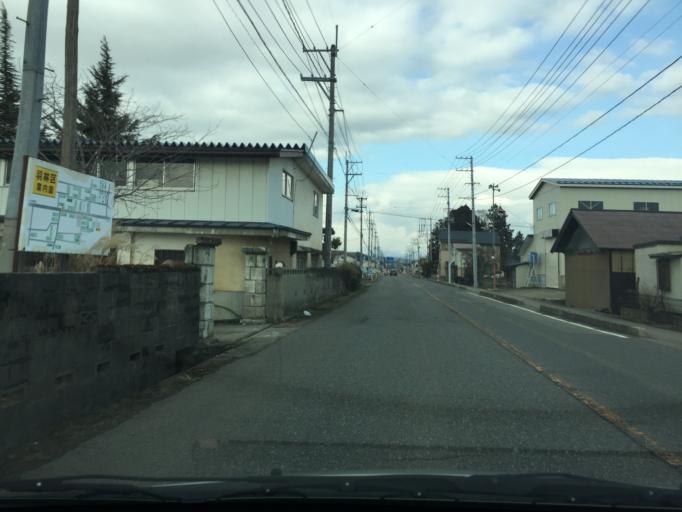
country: JP
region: Fukushima
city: Kitakata
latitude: 37.5534
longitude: 139.8303
